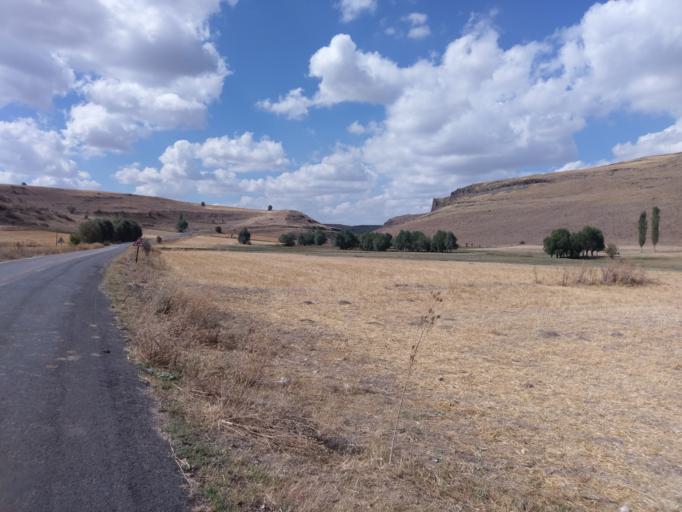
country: TR
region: Kayseri
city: Toklar
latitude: 38.4501
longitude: 36.0670
